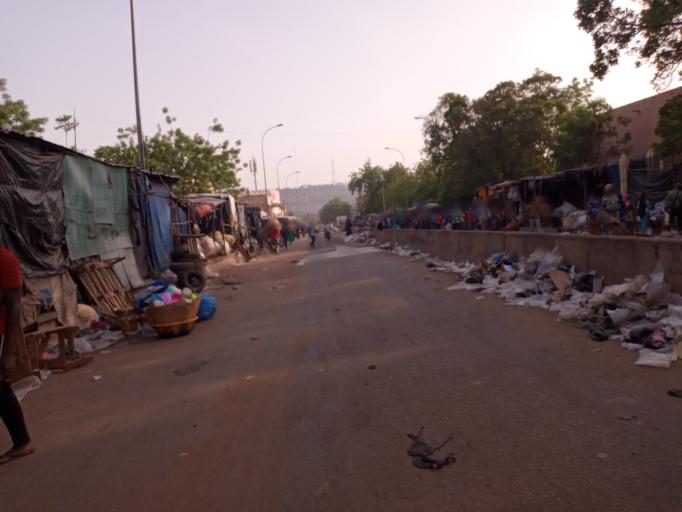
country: ML
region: Bamako
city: Bamako
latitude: 12.6480
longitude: -7.9945
